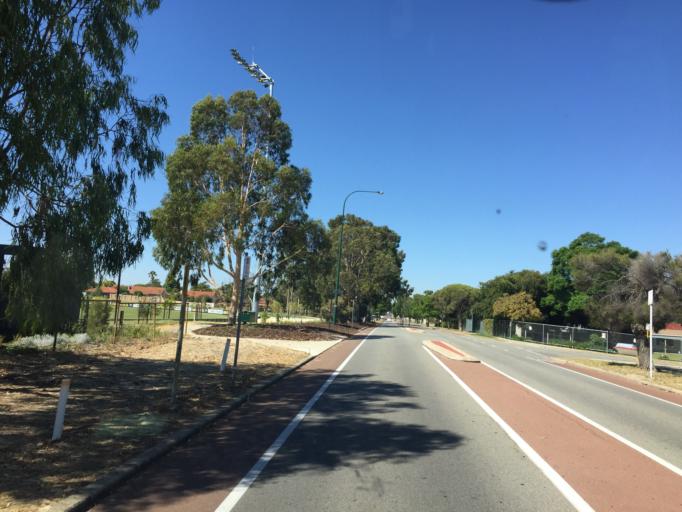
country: AU
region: Western Australia
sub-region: Victoria Park
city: Victoria Park
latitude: -31.9740
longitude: 115.9092
